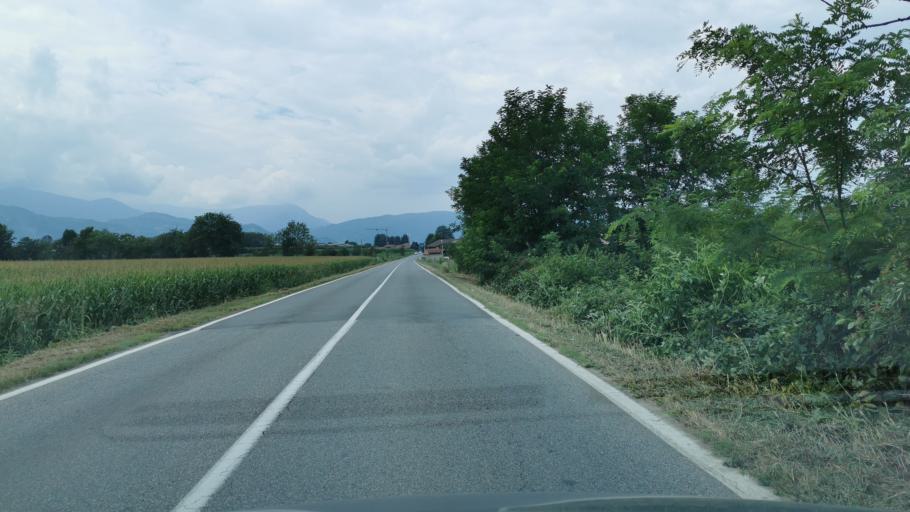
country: IT
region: Piedmont
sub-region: Provincia di Torino
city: Garzigliana
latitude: 44.8359
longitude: 7.3602
